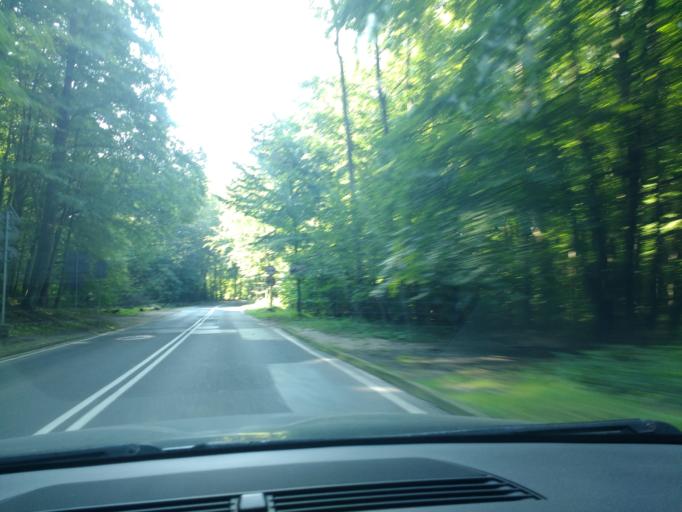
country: PL
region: Pomeranian Voivodeship
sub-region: Gdynia
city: Wielki Kack
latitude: 54.4561
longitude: 18.5214
